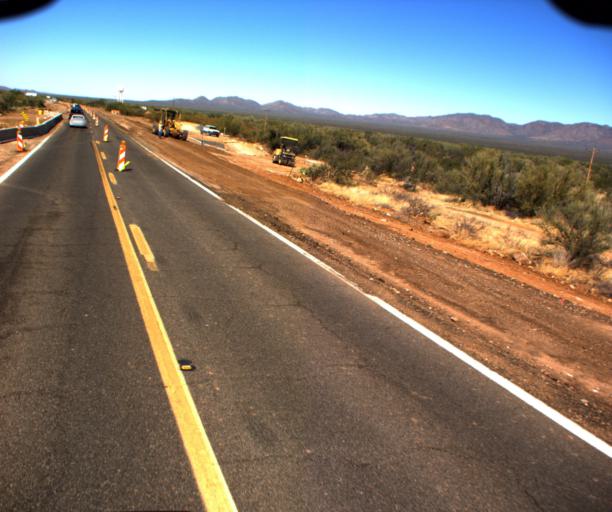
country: US
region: Arizona
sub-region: Pima County
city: Sells
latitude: 31.9959
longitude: -111.6992
